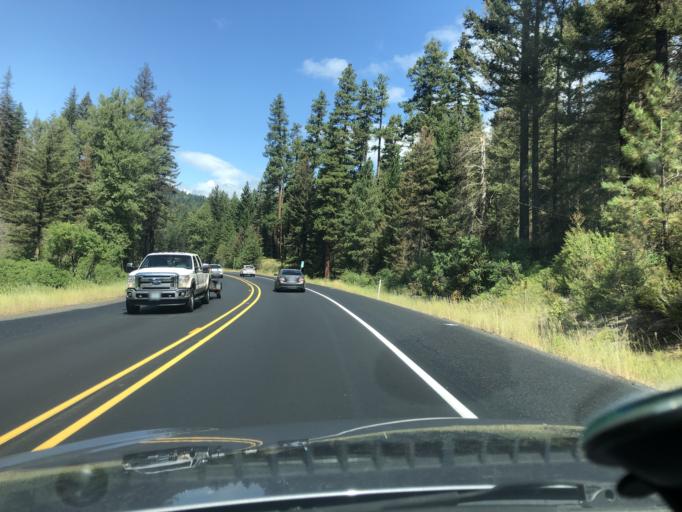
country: US
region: Washington
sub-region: Kittitas County
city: Cle Elum
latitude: 47.2875
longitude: -120.6972
